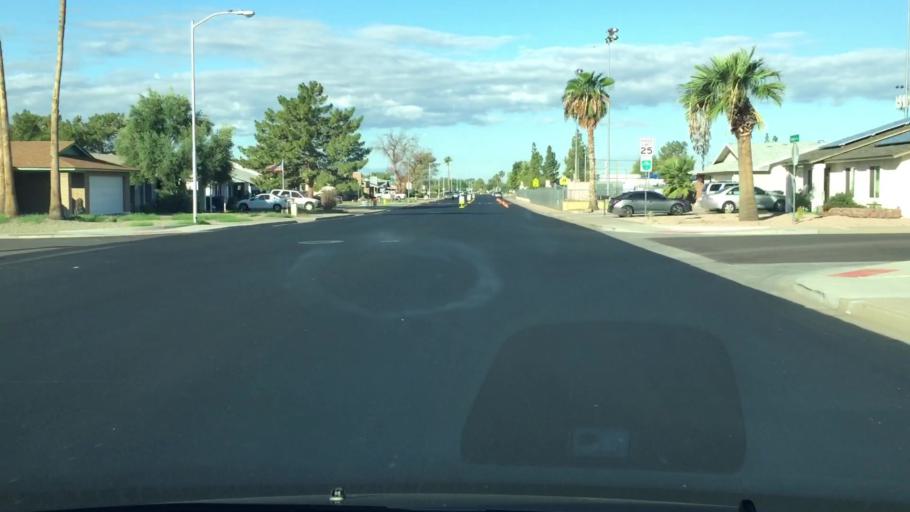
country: US
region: Arizona
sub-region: Maricopa County
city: Gilbert
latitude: 33.4010
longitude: -111.7574
